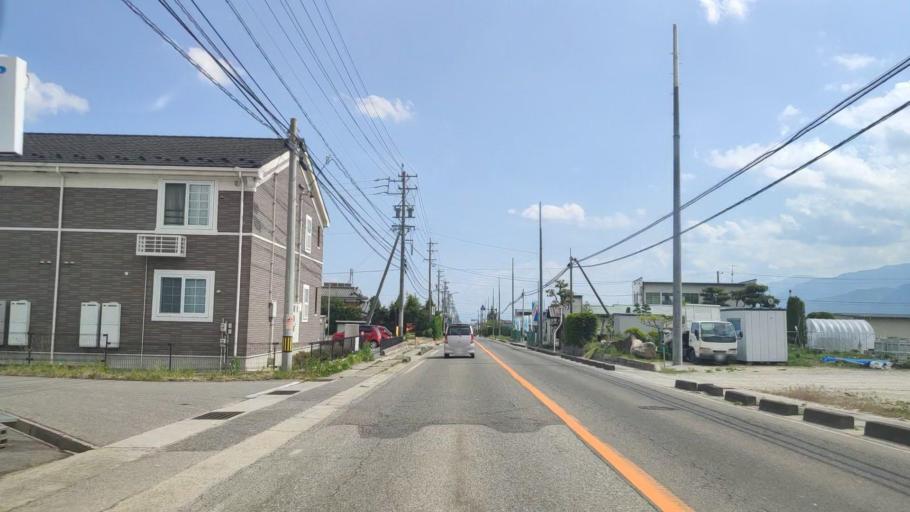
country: JP
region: Nagano
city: Omachi
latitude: 36.4631
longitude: 137.8499
